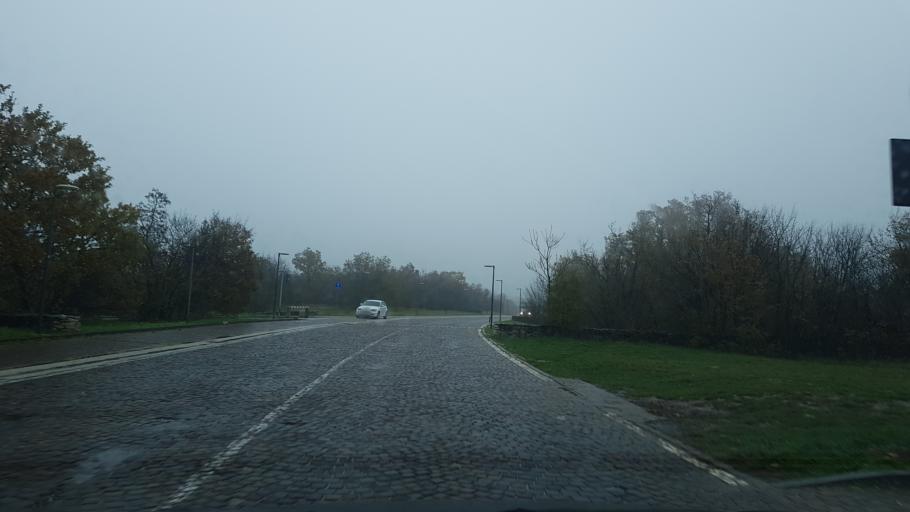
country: IT
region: Friuli Venezia Giulia
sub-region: Provincia di Trieste
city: Domio
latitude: 45.6431
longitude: 13.8490
